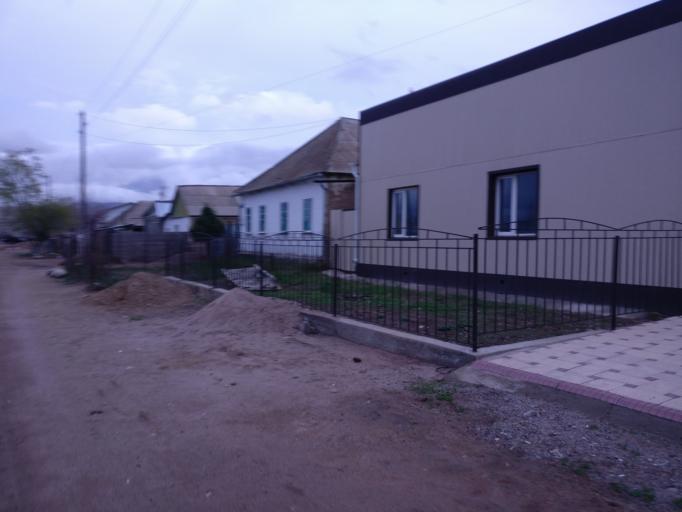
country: KG
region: Ysyk-Koel
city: Bokombayevskoye
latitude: 42.1162
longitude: 76.9896
